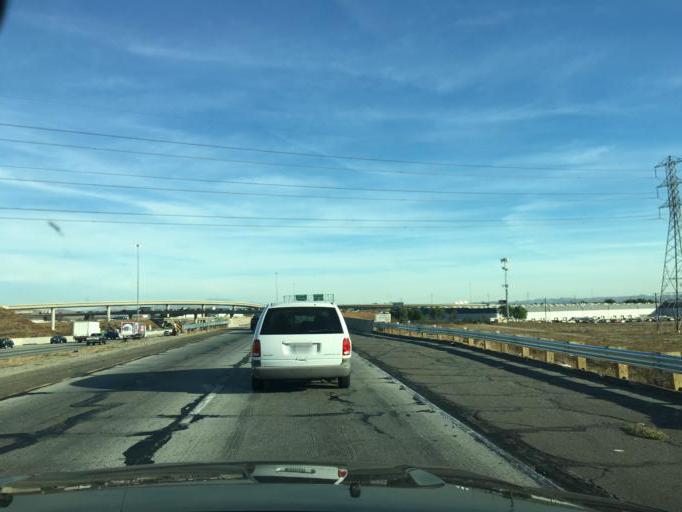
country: US
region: California
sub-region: Riverside County
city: Mira Loma
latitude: 34.0233
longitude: -117.5570
